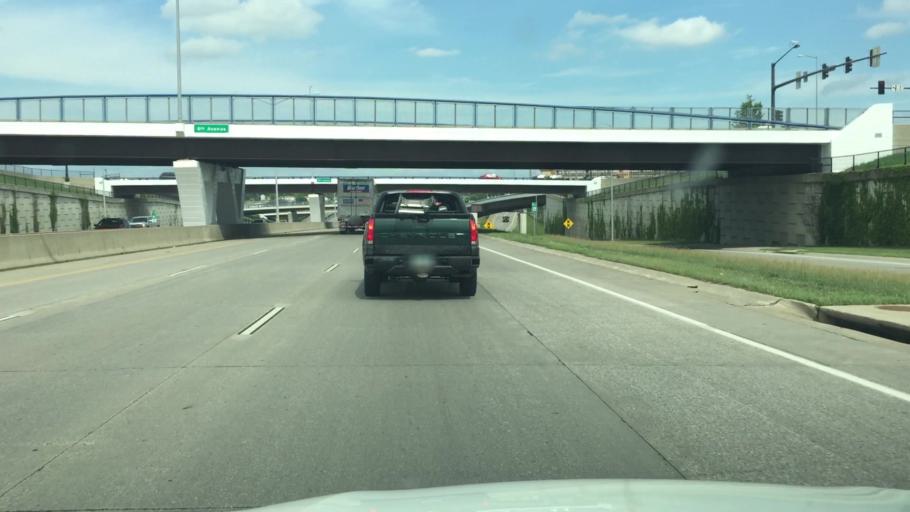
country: US
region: Iowa
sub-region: Polk County
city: Des Moines
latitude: 41.5957
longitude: -93.6265
